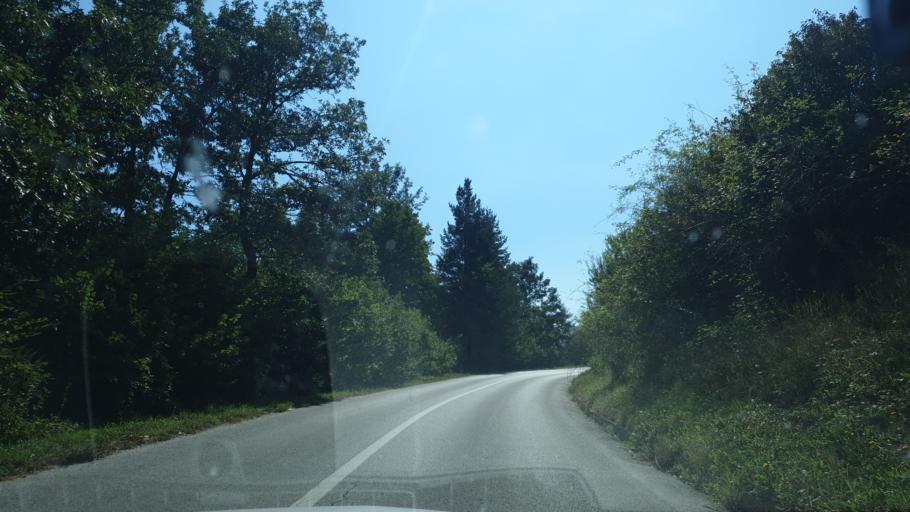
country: RS
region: Central Serbia
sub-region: Zlatiborski Okrug
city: Cajetina
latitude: 43.6676
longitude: 19.8290
